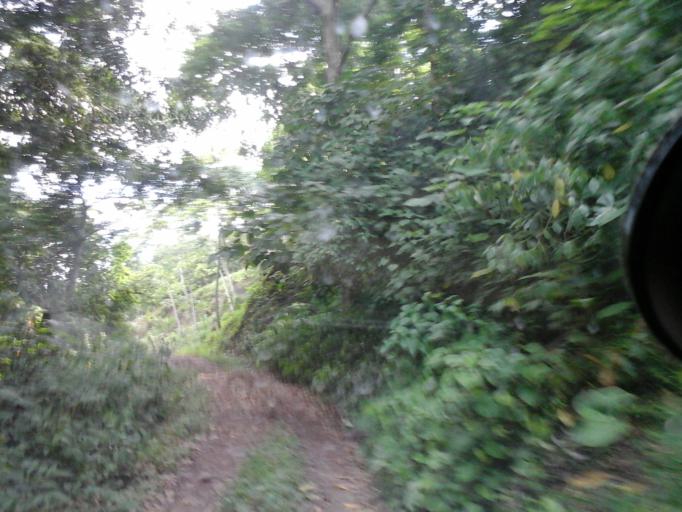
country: CO
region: Cesar
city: San Diego
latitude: 10.2794
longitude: -73.0913
